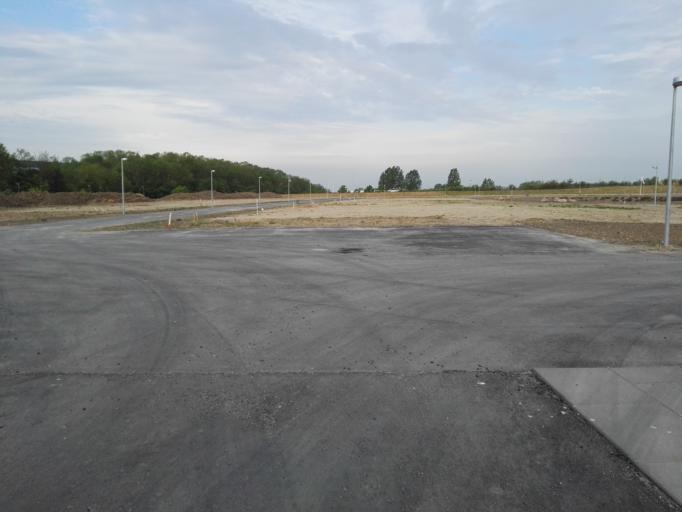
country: DK
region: Capital Region
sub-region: Ballerup Kommune
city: Ballerup
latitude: 55.7295
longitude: 12.3417
